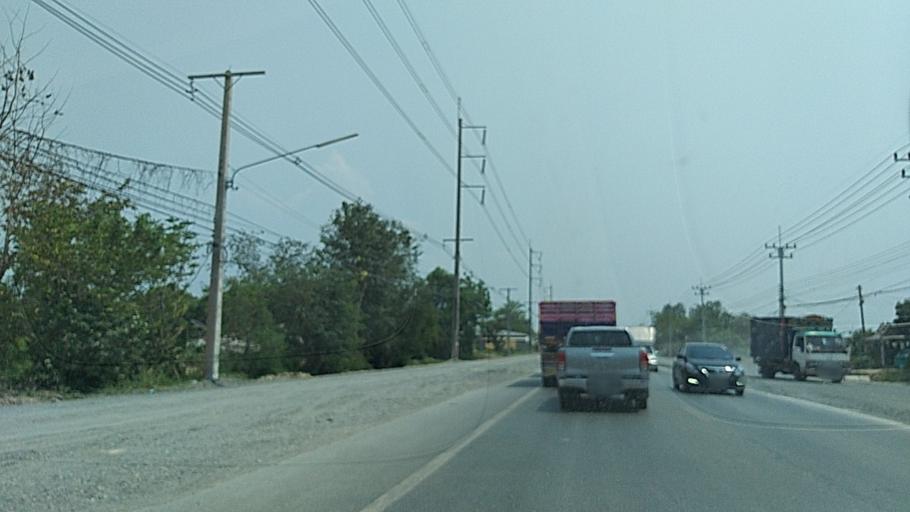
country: TH
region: Chachoengsao
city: Ban Pho
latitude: 13.5539
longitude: 101.1389
